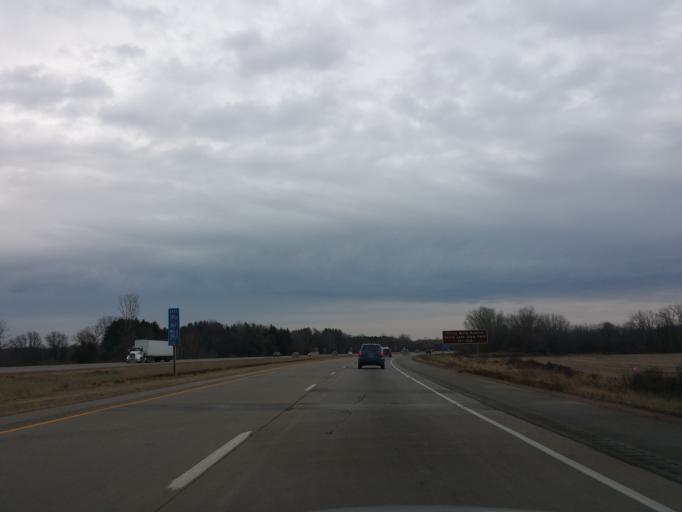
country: US
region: Wisconsin
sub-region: Columbia County
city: Portage
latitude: 43.5212
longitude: -89.5341
